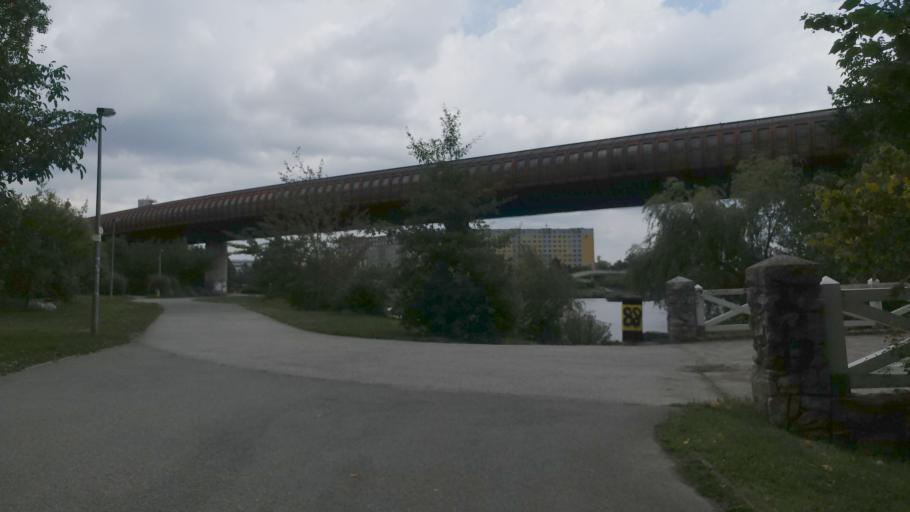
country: CZ
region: Praha
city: Branik
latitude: 50.0480
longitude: 14.3361
